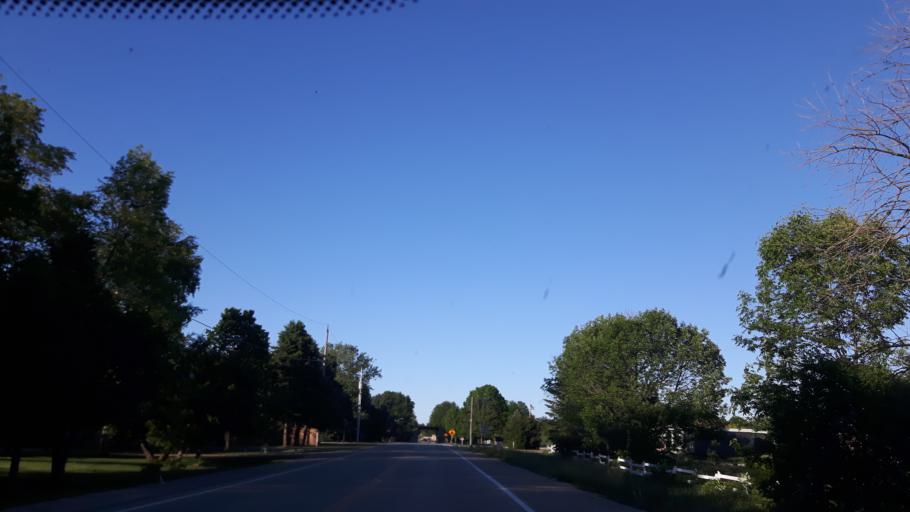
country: CA
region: Ontario
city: Goderich
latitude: 43.6433
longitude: -81.6067
